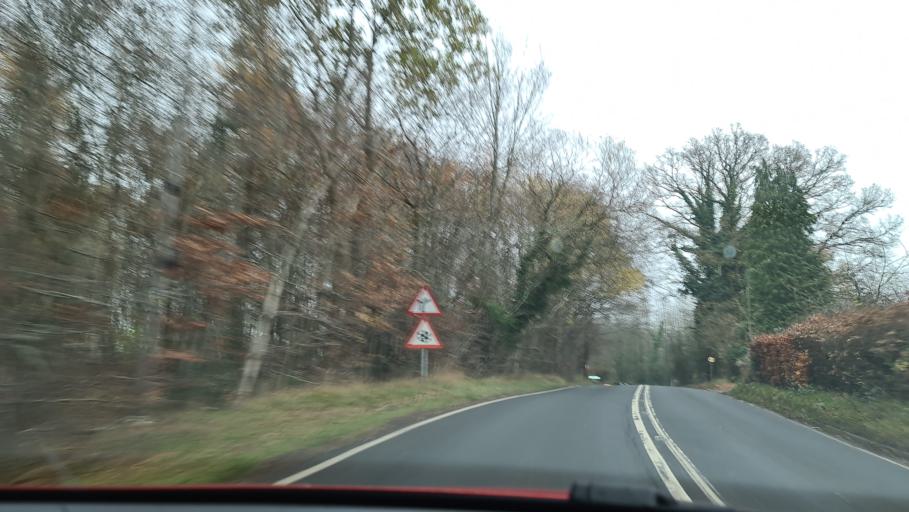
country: GB
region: England
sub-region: Buckinghamshire
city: Beaconsfield
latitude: 51.6293
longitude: -0.6587
